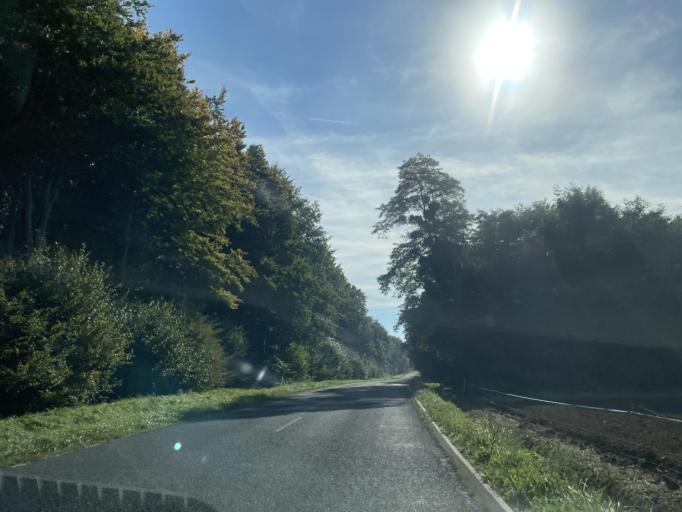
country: FR
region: Ile-de-France
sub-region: Departement de Seine-et-Marne
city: Saint-Jean-les-Deux-Jumeaux
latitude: 48.9202
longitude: 3.0084
